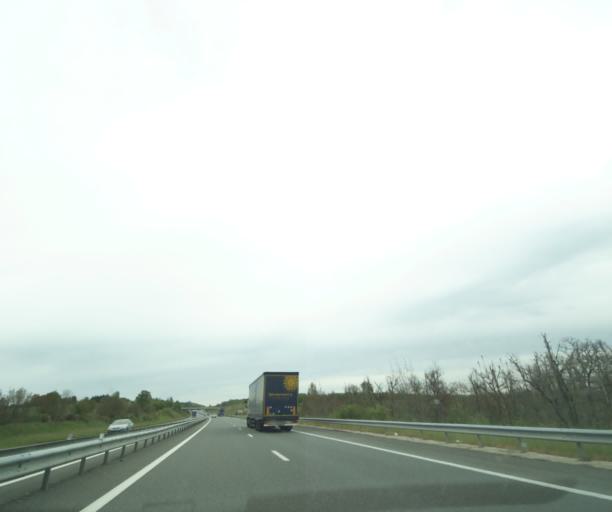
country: FR
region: Midi-Pyrenees
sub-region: Departement du Lot
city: Lalbenque
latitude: 44.2937
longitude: 1.5086
